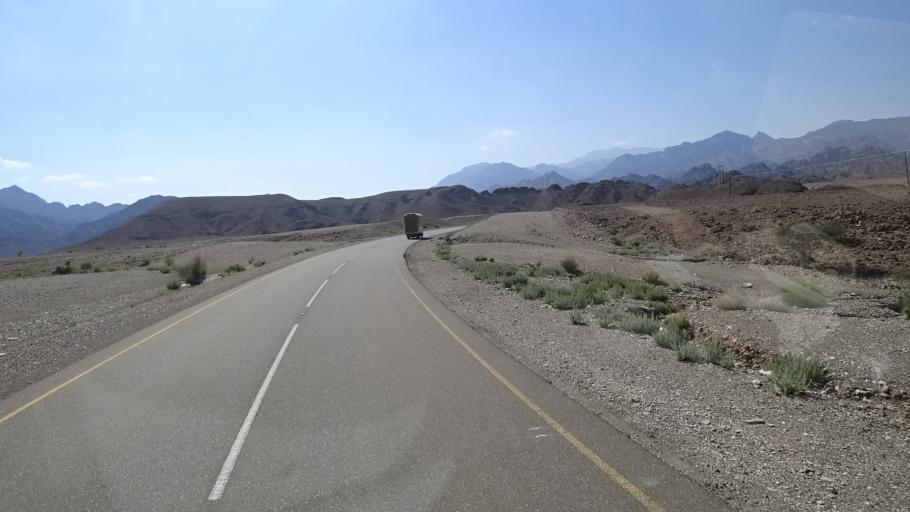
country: OM
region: Al Batinah
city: Al Khaburah
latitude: 23.7530
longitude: 56.9237
